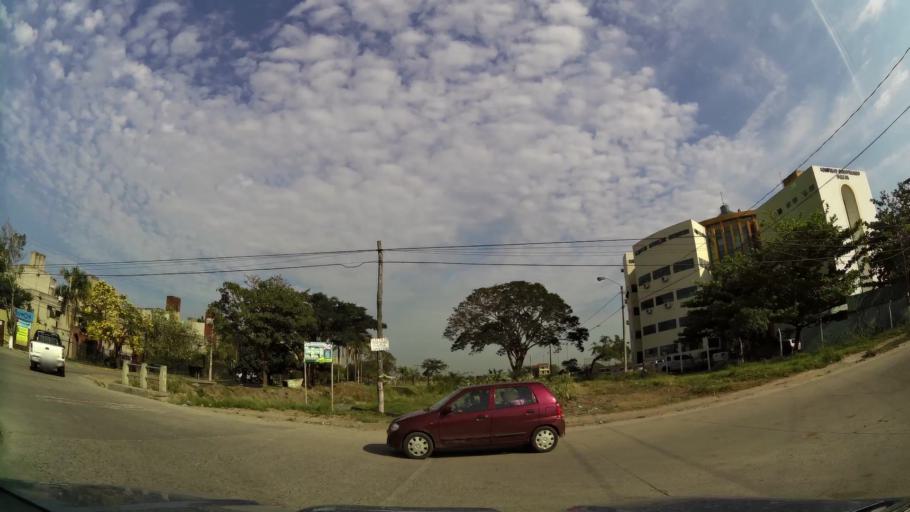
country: BO
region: Santa Cruz
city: Santa Cruz de la Sierra
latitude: -17.7307
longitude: -63.1721
